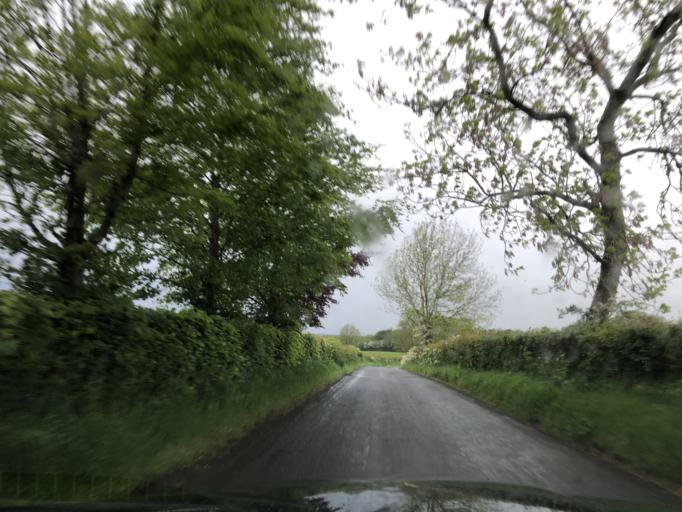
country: GB
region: Northern Ireland
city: Dunloy
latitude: 55.1375
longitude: -6.3740
